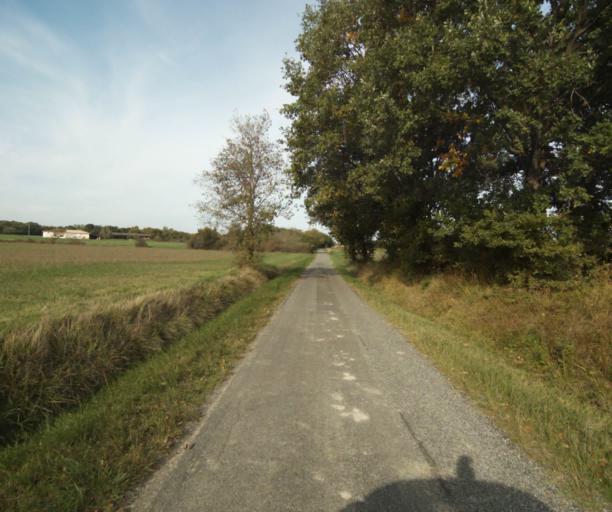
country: FR
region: Midi-Pyrenees
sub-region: Departement du Tarn-et-Garonne
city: Campsas
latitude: 43.9208
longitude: 1.3243
